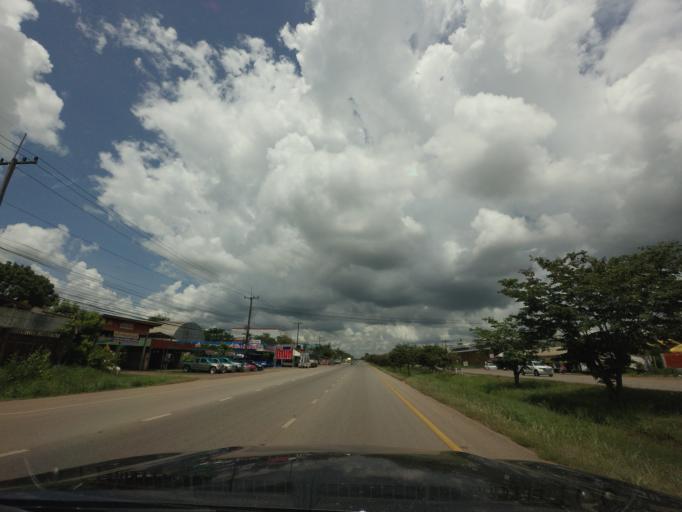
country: TH
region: Changwat Udon Thani
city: Udon Thani
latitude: 17.5326
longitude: 102.7998
